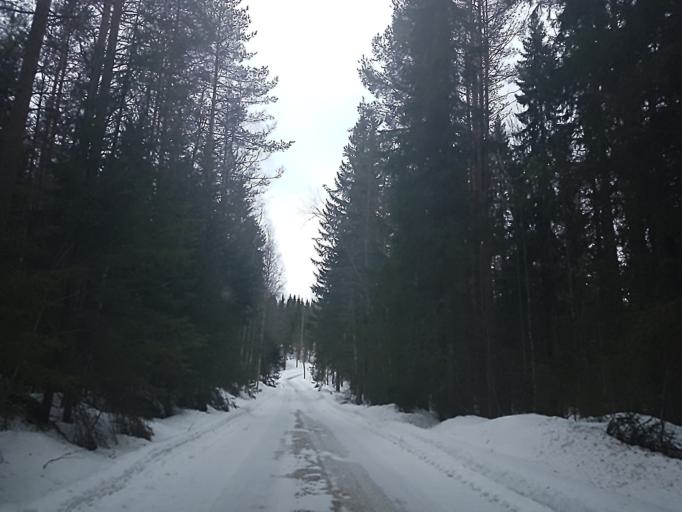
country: FI
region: Northern Savo
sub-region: Koillis-Savo
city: Kaavi
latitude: 62.9789
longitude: 28.7563
